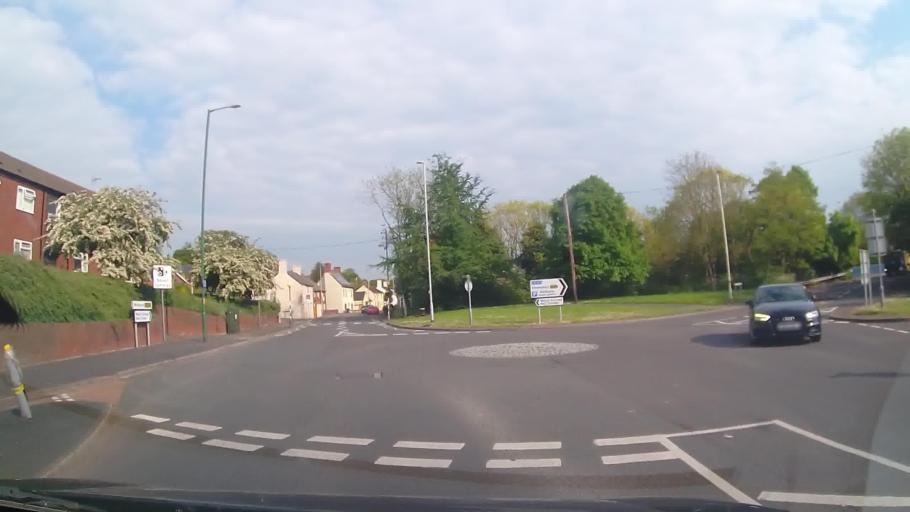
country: GB
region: England
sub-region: Telford and Wrekin
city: Wellington
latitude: 52.7023
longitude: -2.5155
